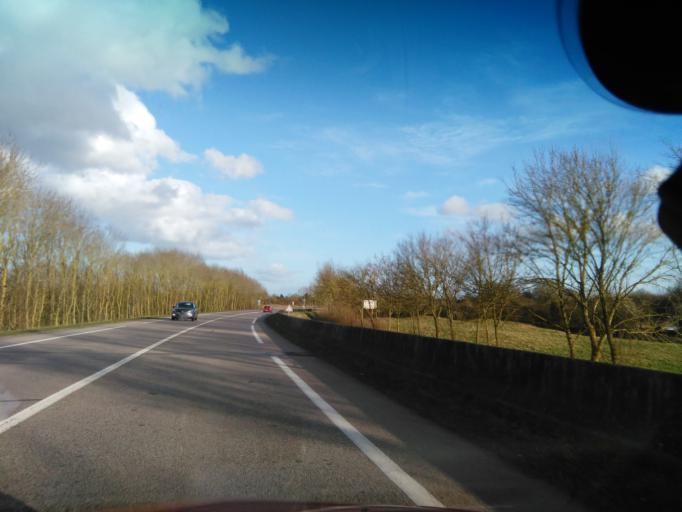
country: FR
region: Lower Normandy
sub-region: Departement du Calvados
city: Falaise
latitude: 48.8831
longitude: -0.2098
